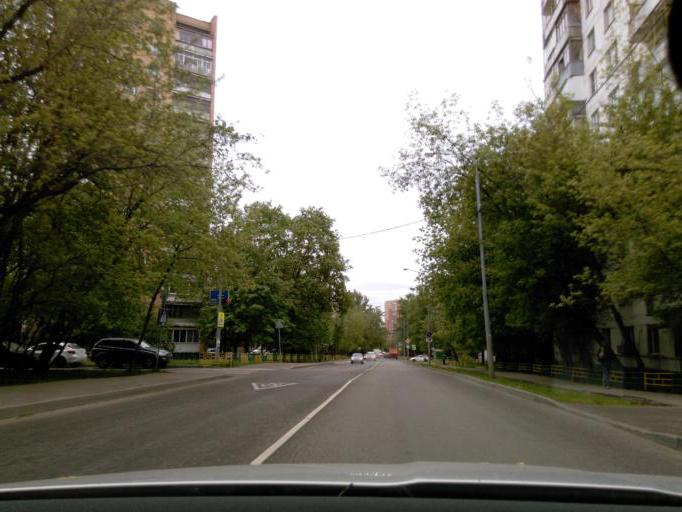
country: RU
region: Moscow
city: Zapadnoye Degunino
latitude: 55.8601
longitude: 37.5189
